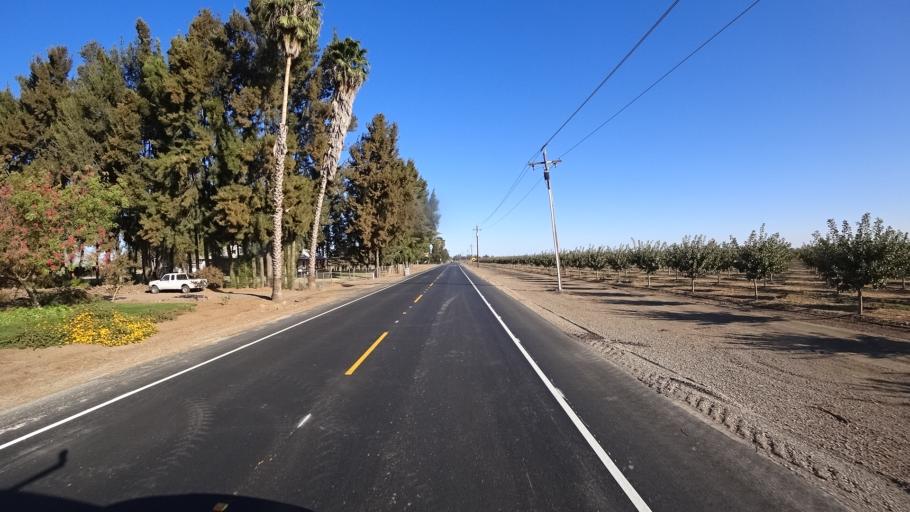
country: US
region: California
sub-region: Yolo County
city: Woodland
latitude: 38.6385
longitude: -121.7846
